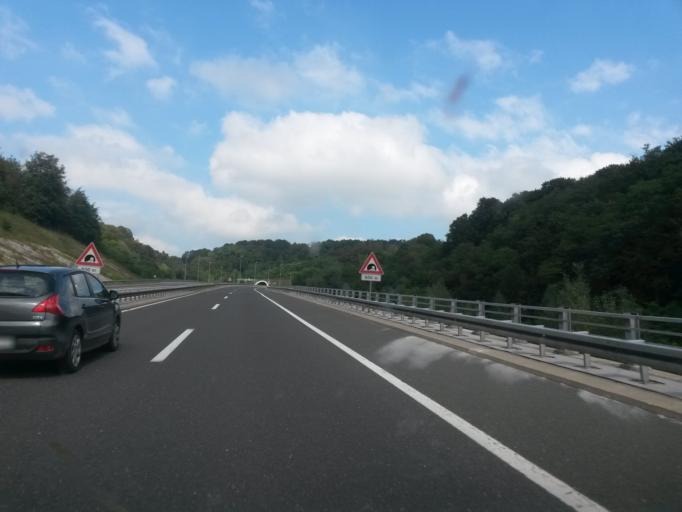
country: HR
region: Varazdinska
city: Ljubescica
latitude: 46.1978
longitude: 16.4116
